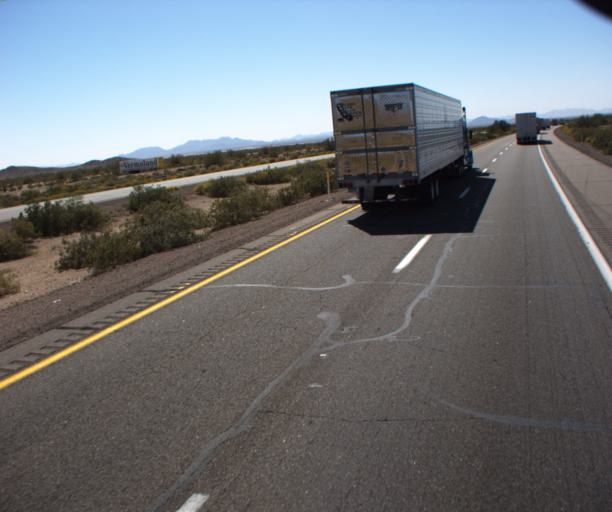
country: US
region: Arizona
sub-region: Yuma County
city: Wellton
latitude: 32.7234
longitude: -113.7598
